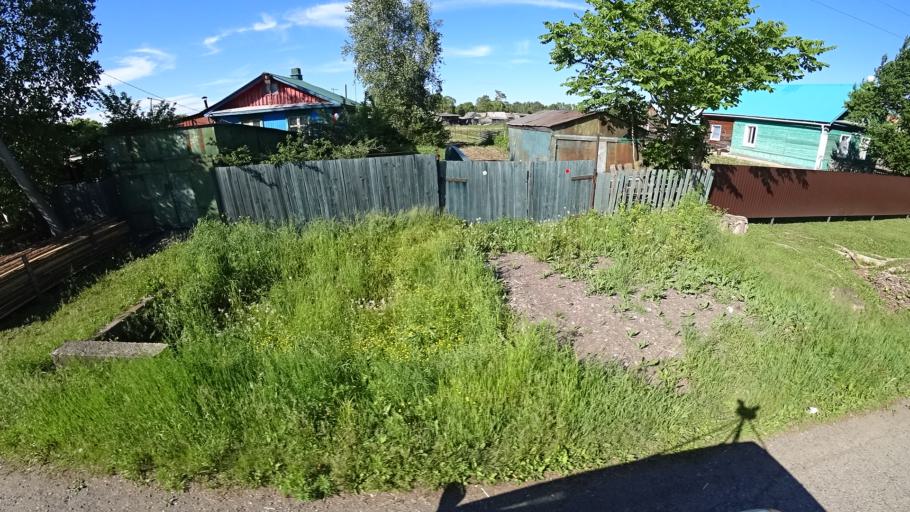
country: RU
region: Khabarovsk Krai
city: Khor
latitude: 47.8864
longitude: 134.9947
